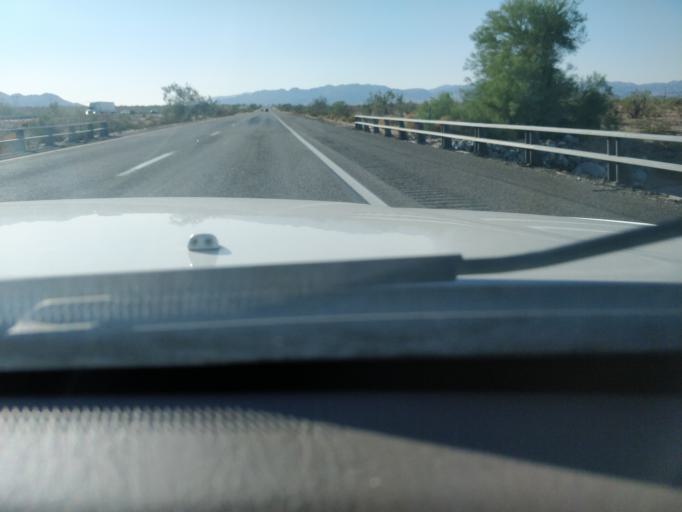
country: US
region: California
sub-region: Imperial County
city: Niland
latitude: 33.7032
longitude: -115.3204
